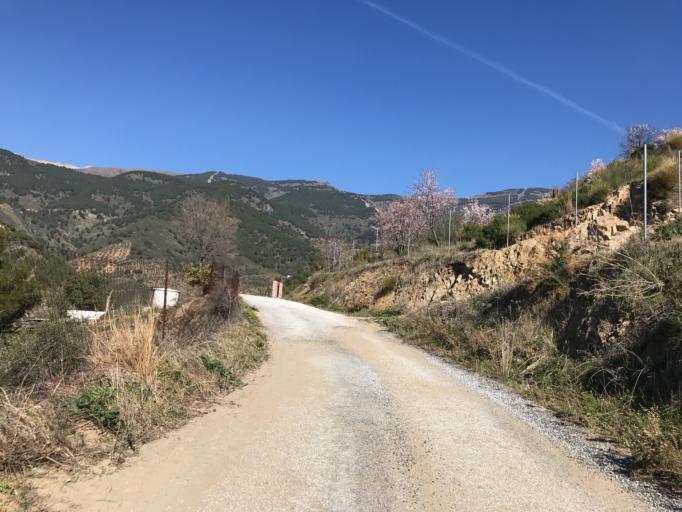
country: ES
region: Andalusia
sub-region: Provincia de Malaga
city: Canillas de Albaida
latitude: 36.8524
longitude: -3.9891
